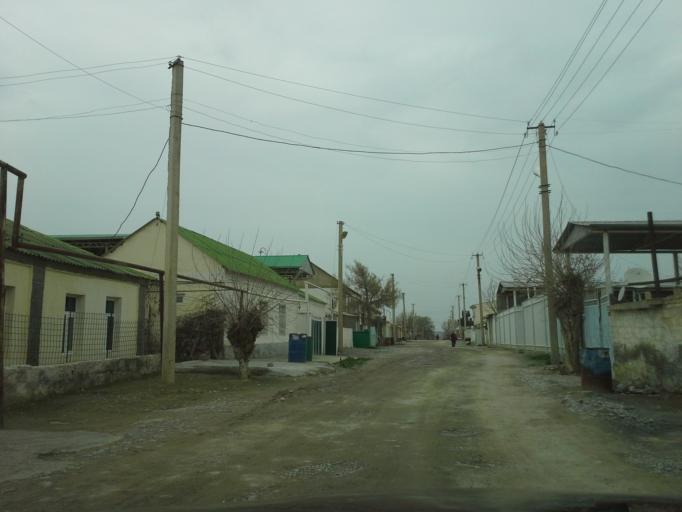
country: TM
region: Ahal
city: Abadan
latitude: 37.9757
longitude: 58.2195
